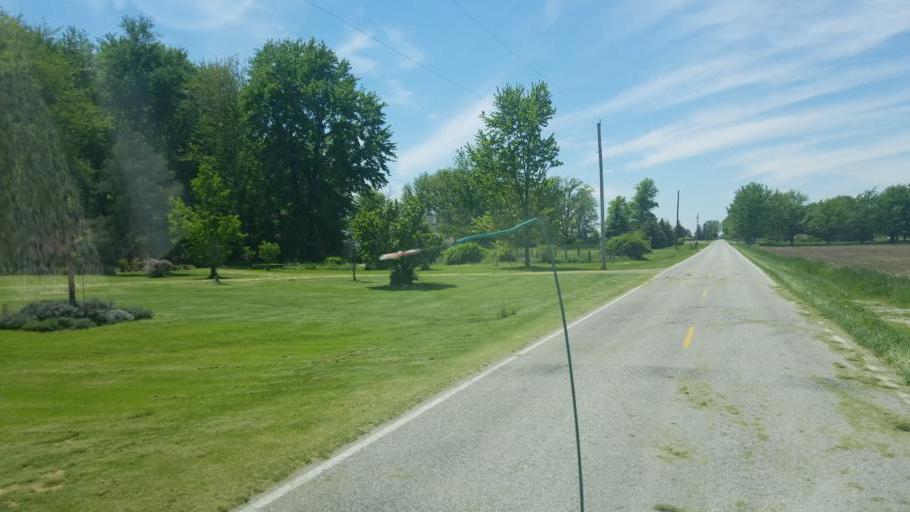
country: US
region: Ohio
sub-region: Huron County
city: Norwalk
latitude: 41.1892
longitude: -82.5485
